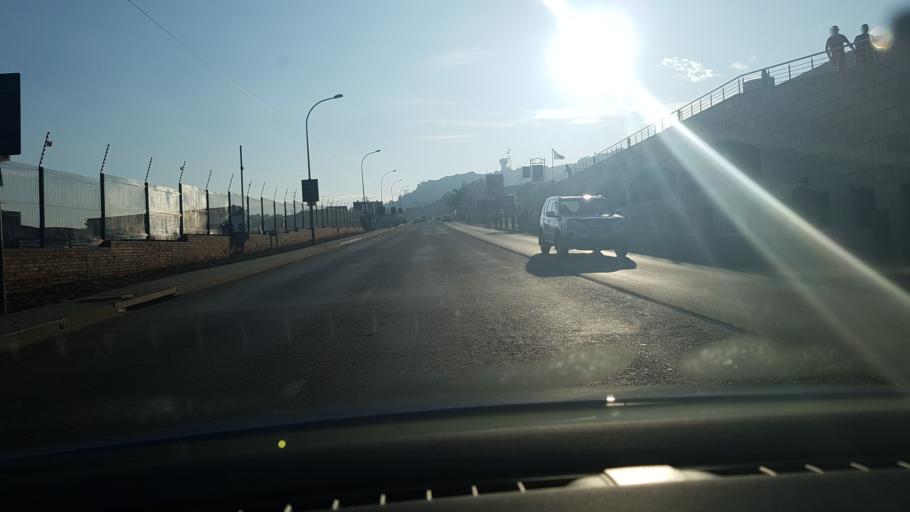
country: ZA
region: Gauteng
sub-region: Ekurhuleni Metropolitan Municipality
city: Germiston
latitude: -26.1680
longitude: 28.1633
